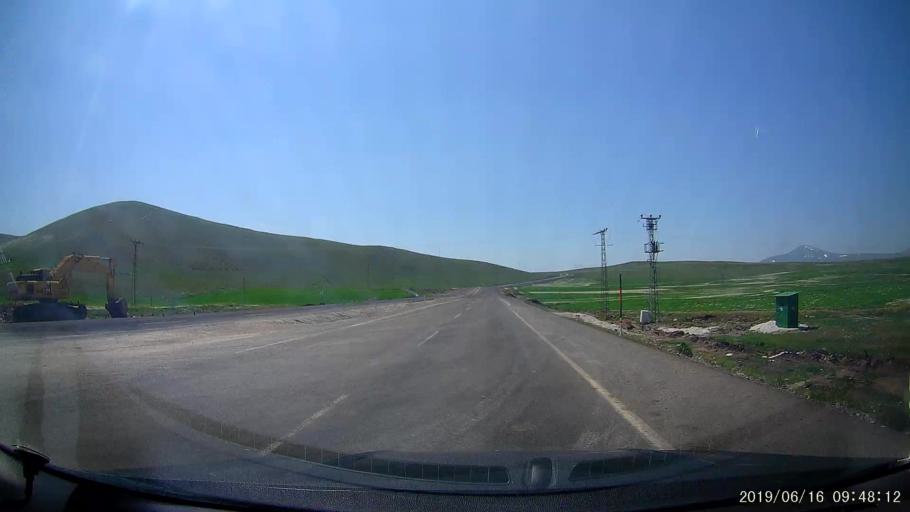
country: TR
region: Kars
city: Digor
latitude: 40.4364
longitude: 43.3515
